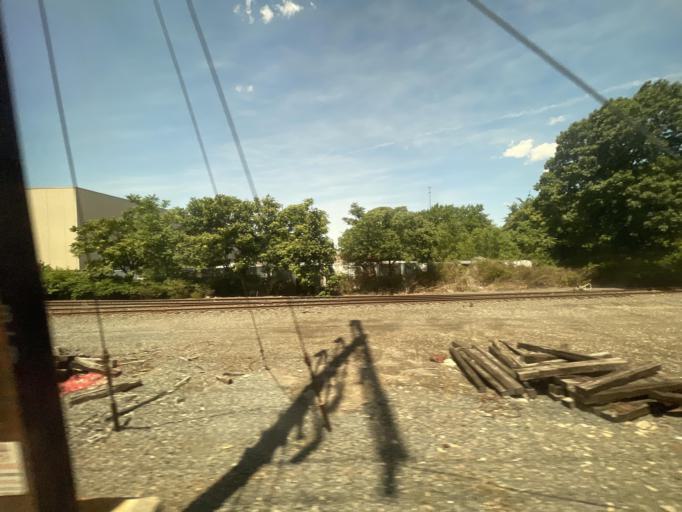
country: US
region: New Jersey
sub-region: Middlesex County
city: New Brunswick
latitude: 40.4744
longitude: -74.4701
